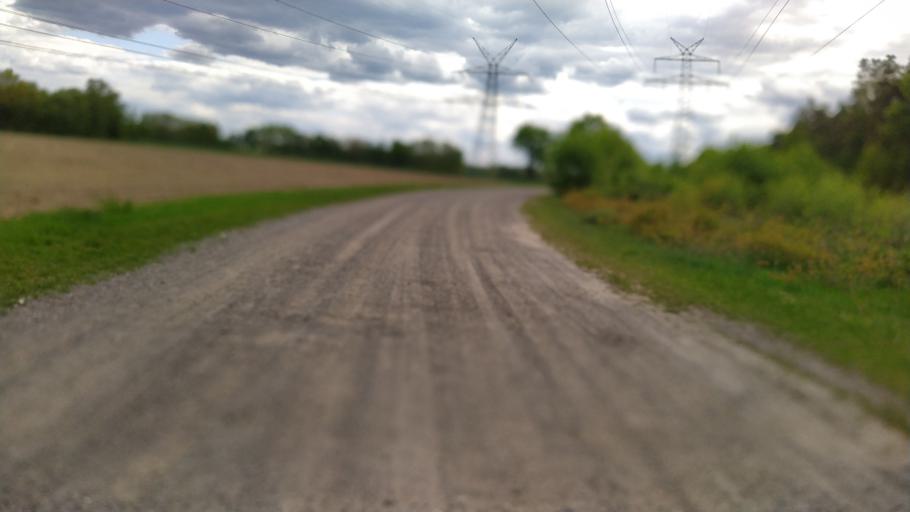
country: DE
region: Lower Saxony
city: Ahlerstedt
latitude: 53.3678
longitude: 9.3944
